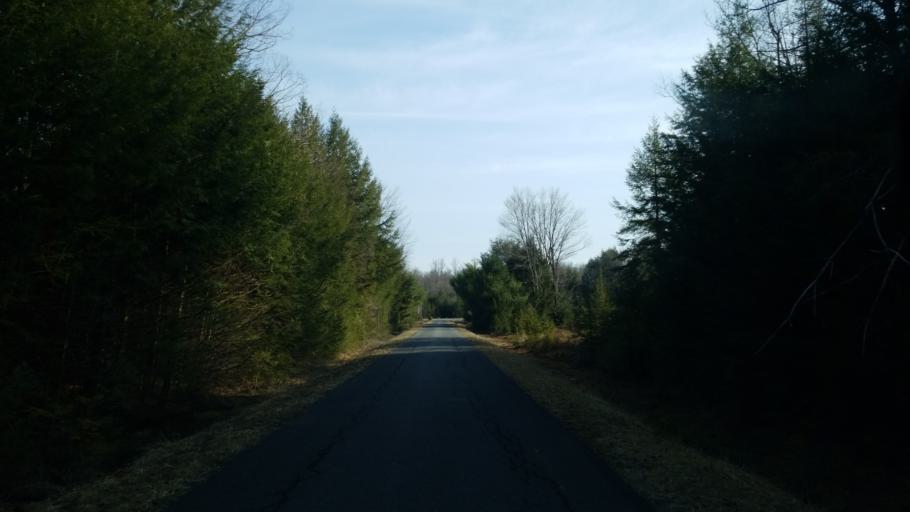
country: US
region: Pennsylvania
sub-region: Clearfield County
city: Shiloh
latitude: 41.2368
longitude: -78.2083
